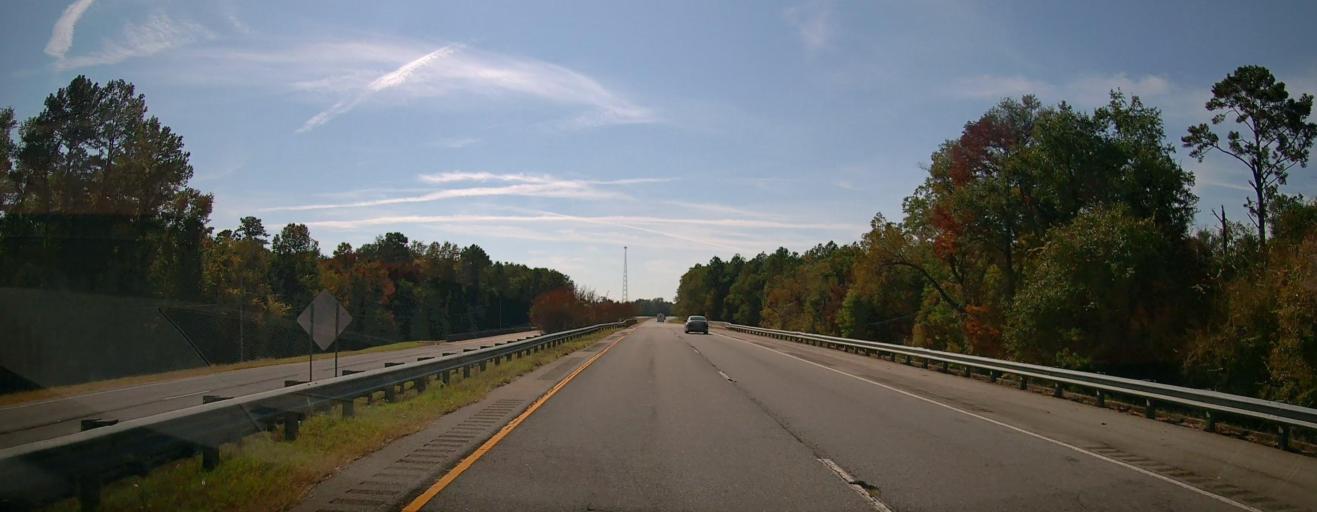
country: US
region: Georgia
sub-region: Lee County
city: Leesburg
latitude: 31.7602
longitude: -83.9768
